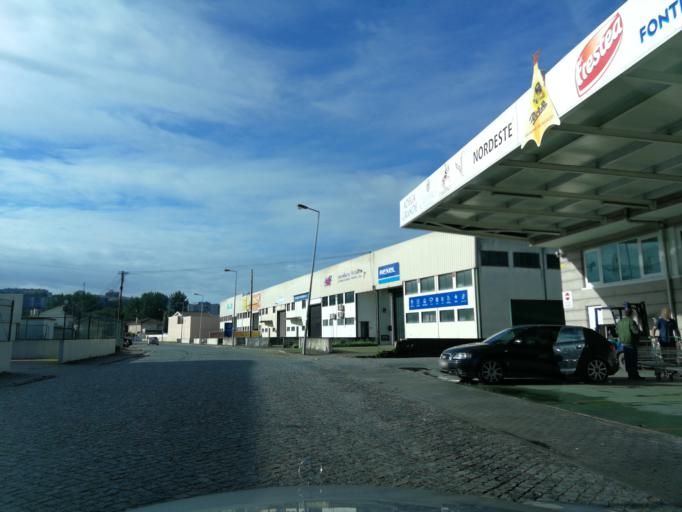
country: PT
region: Braga
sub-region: Braga
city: Braga
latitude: 41.5636
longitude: -8.4449
